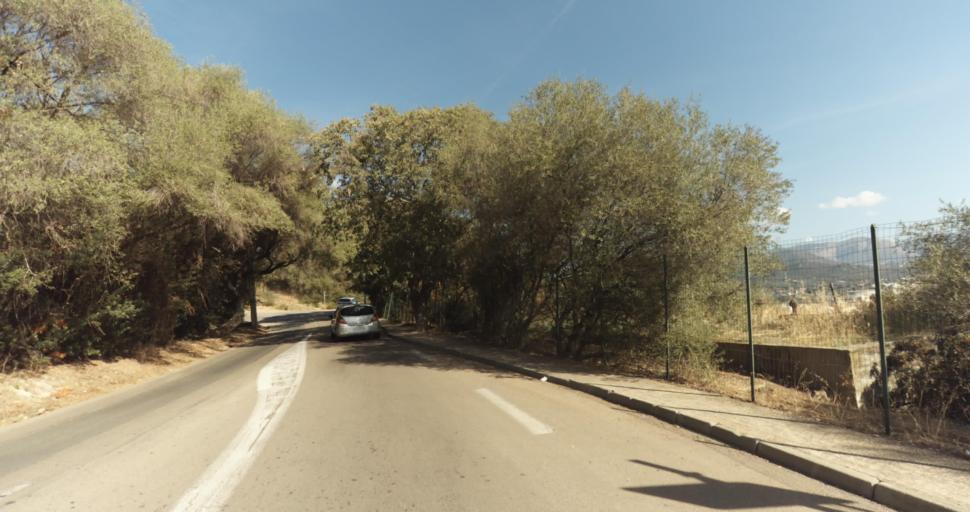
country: FR
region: Corsica
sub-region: Departement de la Corse-du-Sud
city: Ajaccio
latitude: 41.9228
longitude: 8.7308
